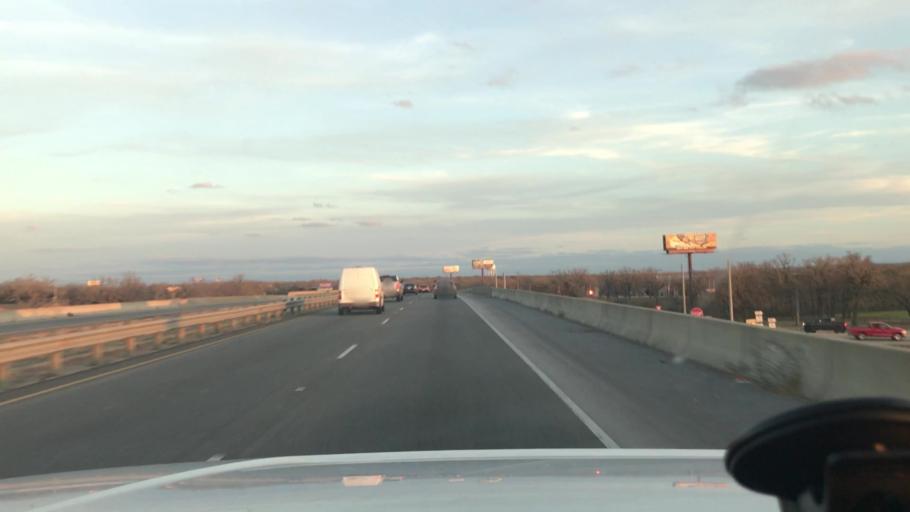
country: US
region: Texas
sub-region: Bastrop County
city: Wyldwood
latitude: 30.1129
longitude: -97.4163
